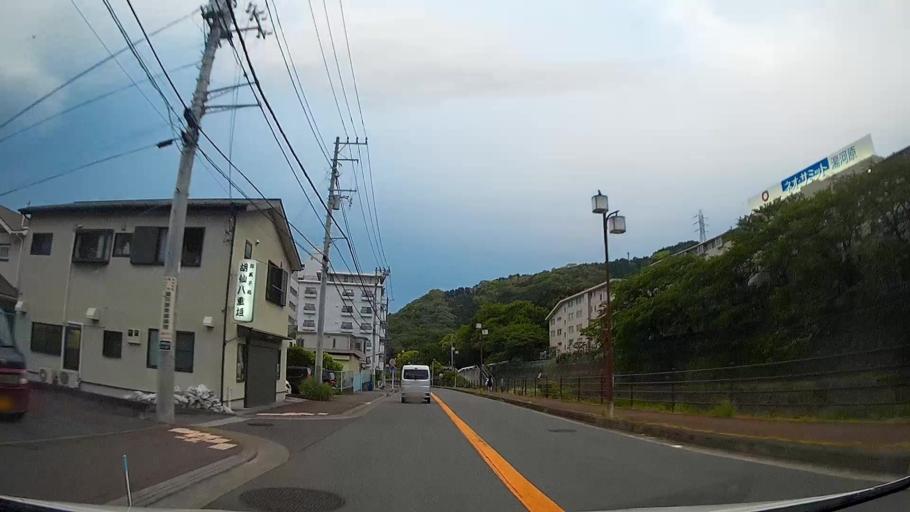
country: JP
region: Kanagawa
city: Yugawara
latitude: 35.1408
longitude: 139.0966
